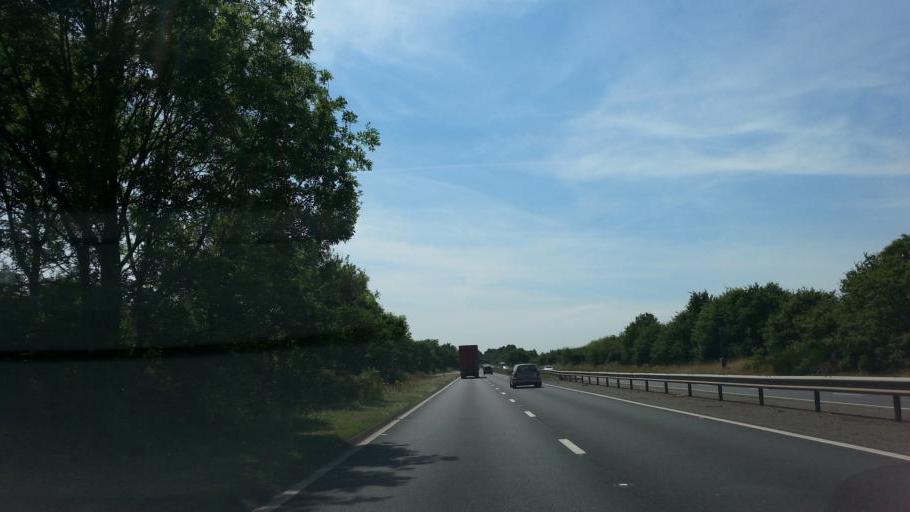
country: GB
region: England
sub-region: Staffordshire
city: Lichfield
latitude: 52.6614
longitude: -1.8163
